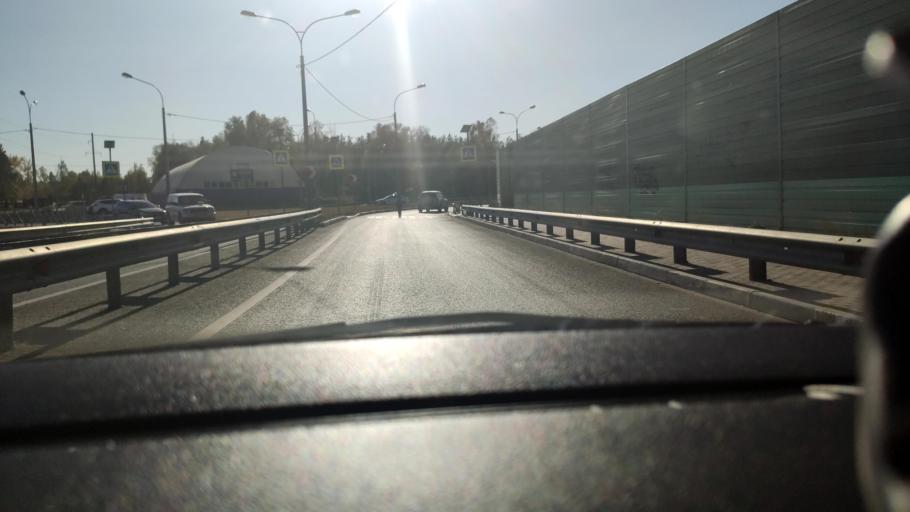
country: RU
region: Voronezj
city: Pridonskoy
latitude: 51.6851
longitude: 39.1179
